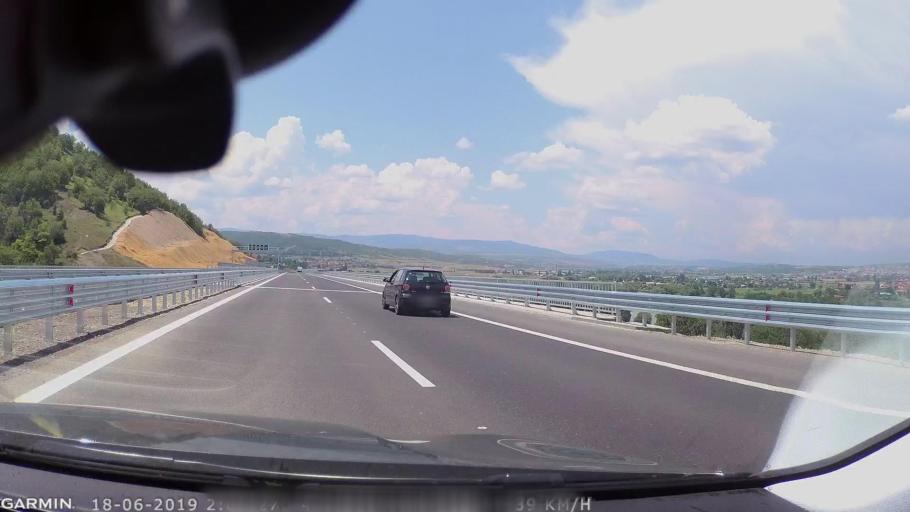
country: BG
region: Blagoevgrad
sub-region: Obshtina Blagoevgrad
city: Blagoevgrad
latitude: 41.9717
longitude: 23.0819
